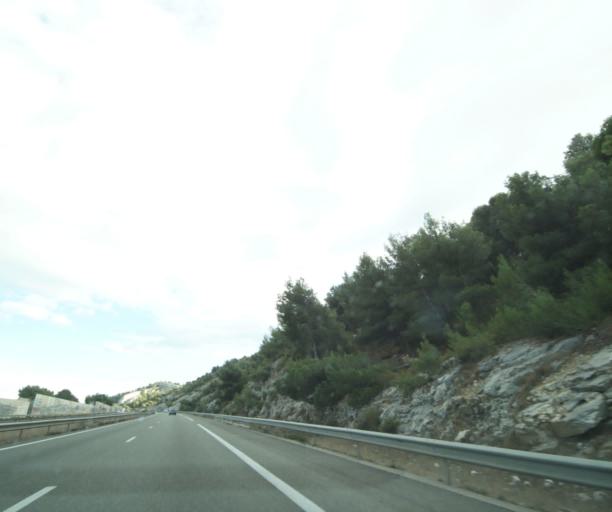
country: FR
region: Provence-Alpes-Cote d'Azur
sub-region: Departement des Bouches-du-Rhone
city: Chateauneuf-les-Martigues
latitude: 43.3833
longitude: 5.1532
